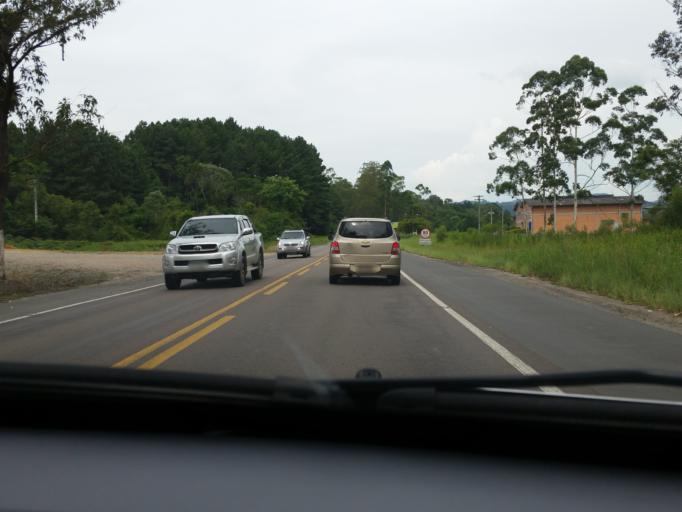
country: BR
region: Santa Catarina
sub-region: Rio Do Sul
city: Rio do Sul
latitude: -27.1717
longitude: -49.5798
